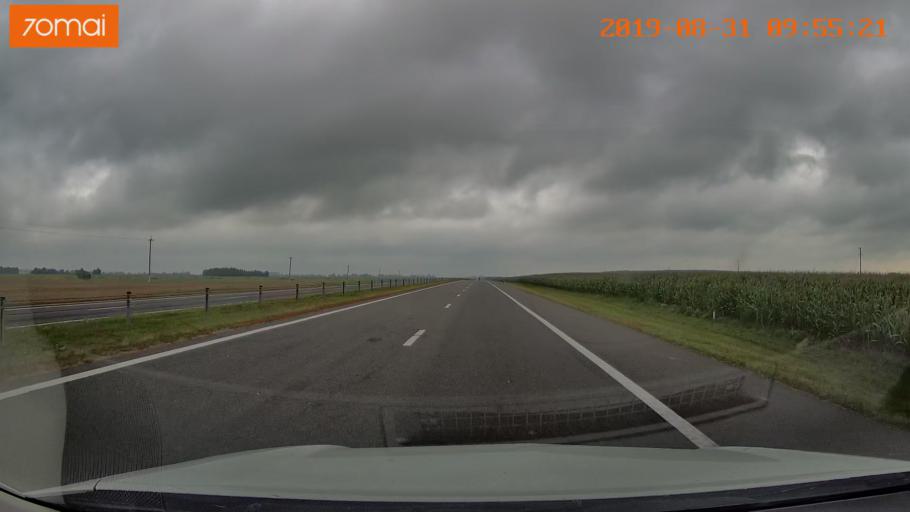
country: BY
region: Mogilev
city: Vishow
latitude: 53.9829
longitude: 29.8671
